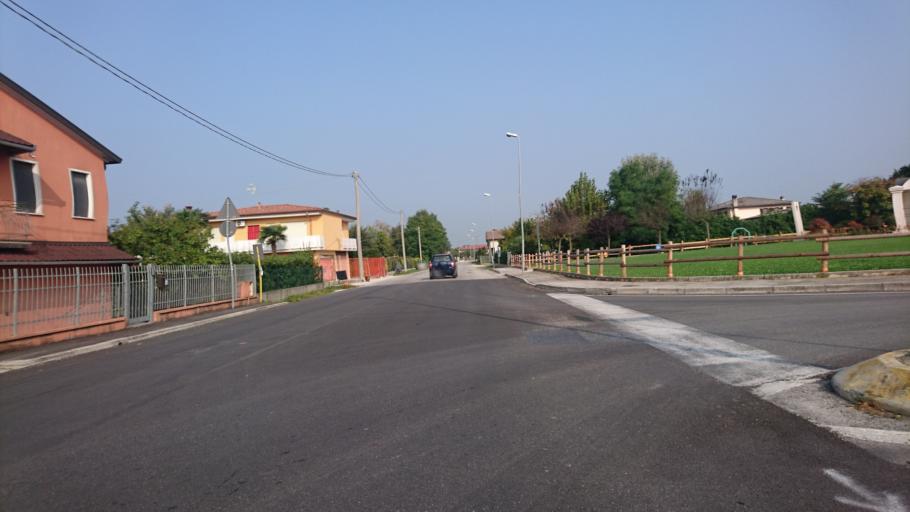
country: IT
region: Veneto
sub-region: Provincia di Padova
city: Pieve
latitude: 45.5383
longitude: 11.8344
